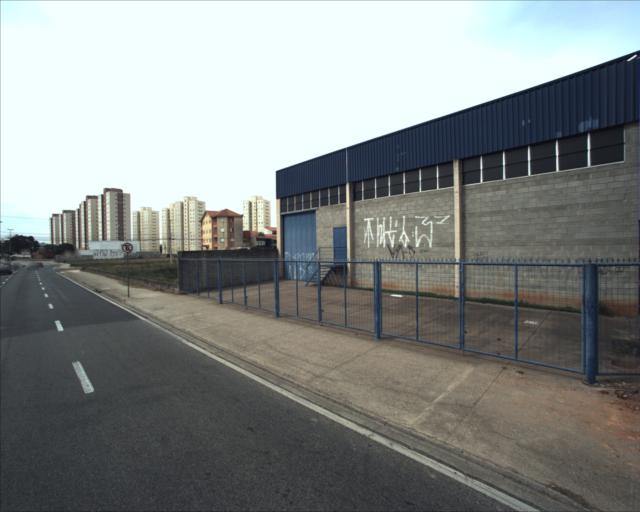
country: BR
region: Sao Paulo
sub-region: Sorocaba
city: Sorocaba
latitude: -23.4793
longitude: -47.4565
